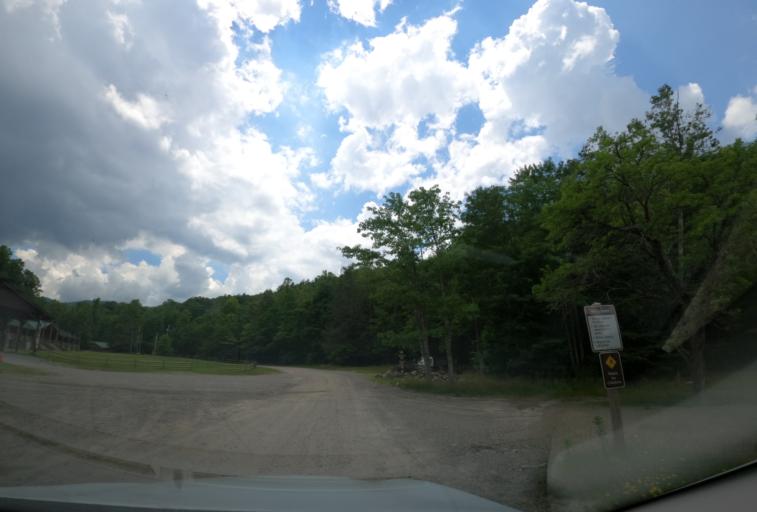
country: US
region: North Carolina
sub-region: Haywood County
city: Hazelwood
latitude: 35.3900
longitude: -82.8974
